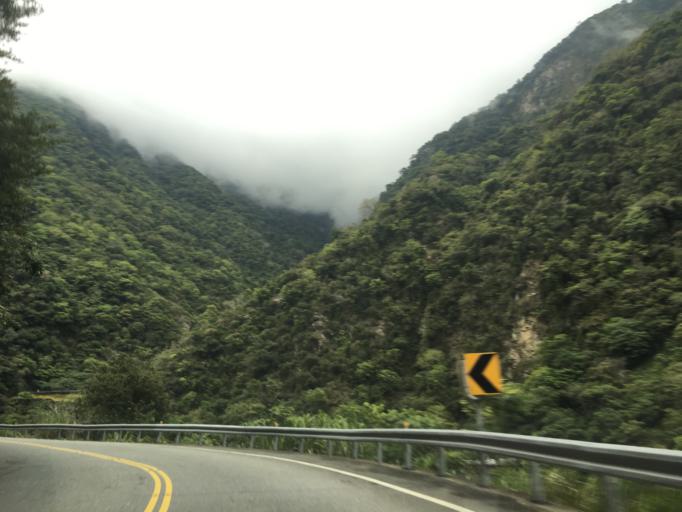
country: TW
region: Taiwan
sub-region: Hualien
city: Hualian
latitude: 24.1769
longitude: 121.5871
